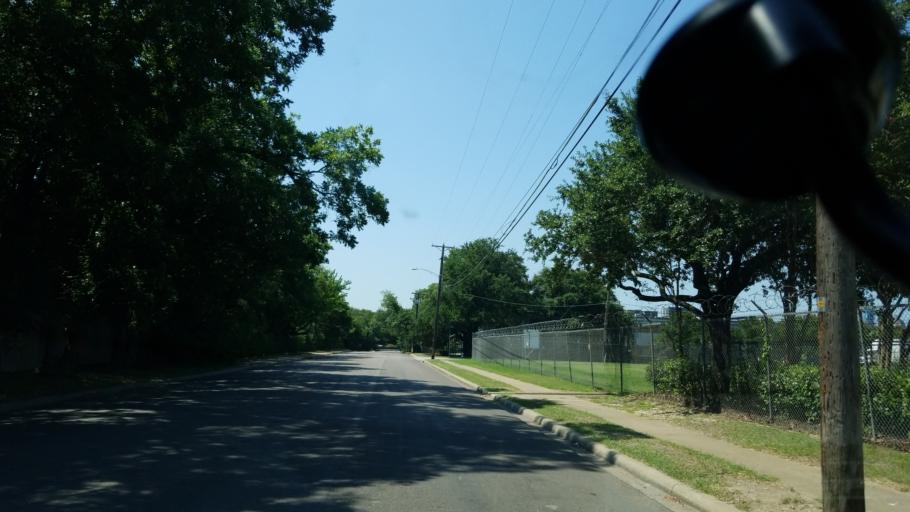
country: US
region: Texas
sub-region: Dallas County
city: Cockrell Hill
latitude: 32.7163
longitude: -96.8658
